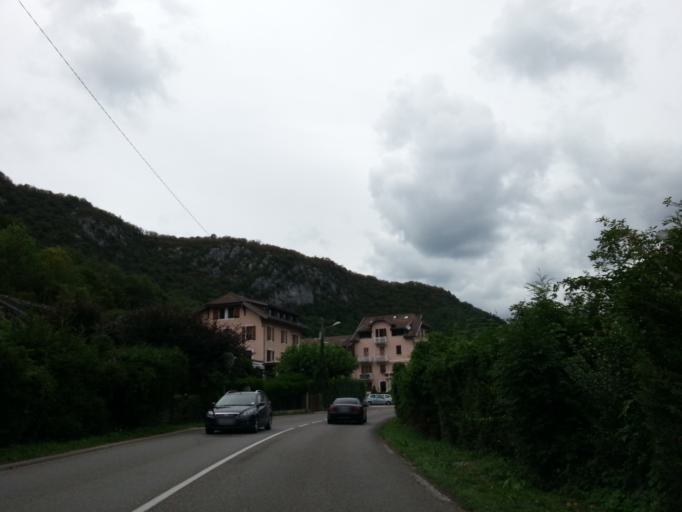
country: FR
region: Rhone-Alpes
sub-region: Departement de la Haute-Savoie
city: Talloires
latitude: 45.8151
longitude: 6.2086
